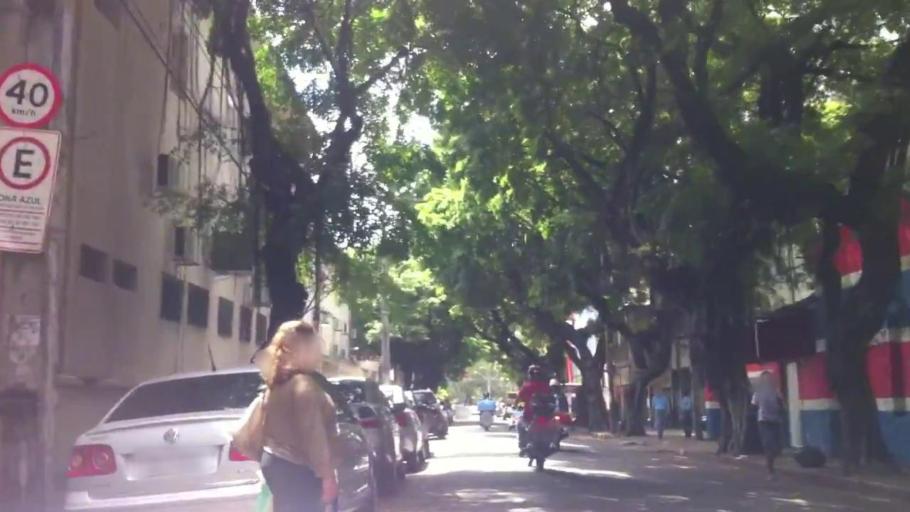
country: BR
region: Pernambuco
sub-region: Recife
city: Recife
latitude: -8.0589
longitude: -34.8842
